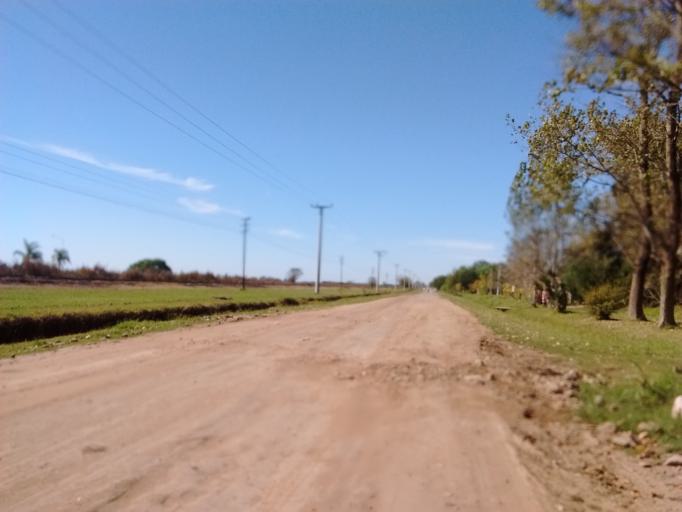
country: AR
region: Santa Fe
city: Funes
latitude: -32.9088
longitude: -60.8582
